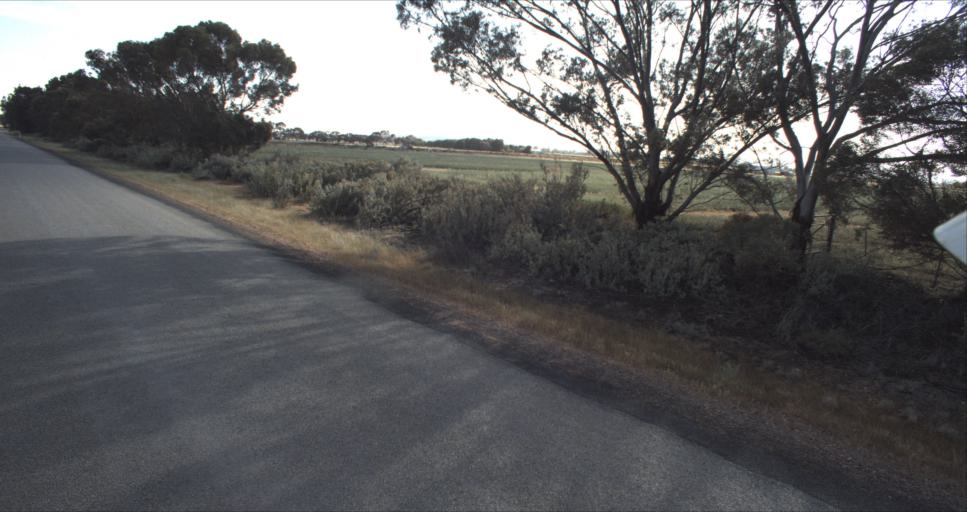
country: AU
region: New South Wales
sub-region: Leeton
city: Leeton
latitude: -34.5058
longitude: 146.3932
